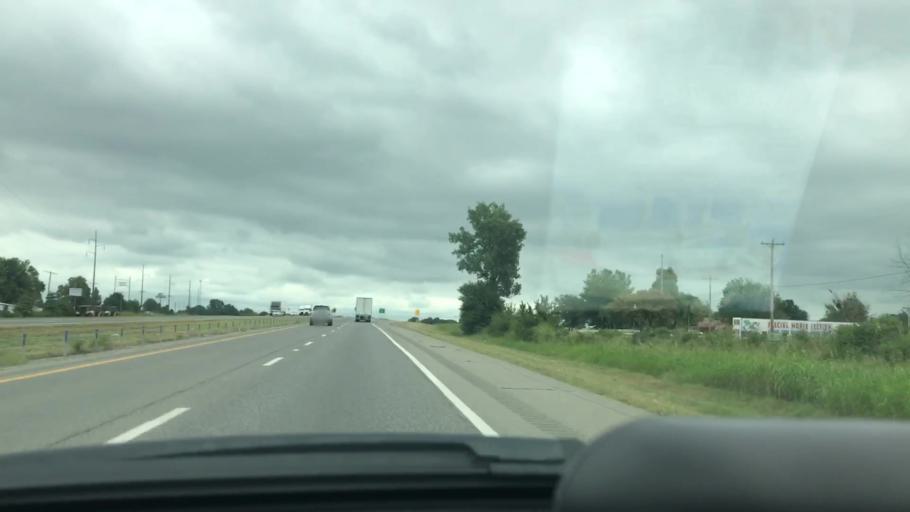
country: US
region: Oklahoma
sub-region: McIntosh County
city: Eufaula
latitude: 35.3574
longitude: -95.5753
